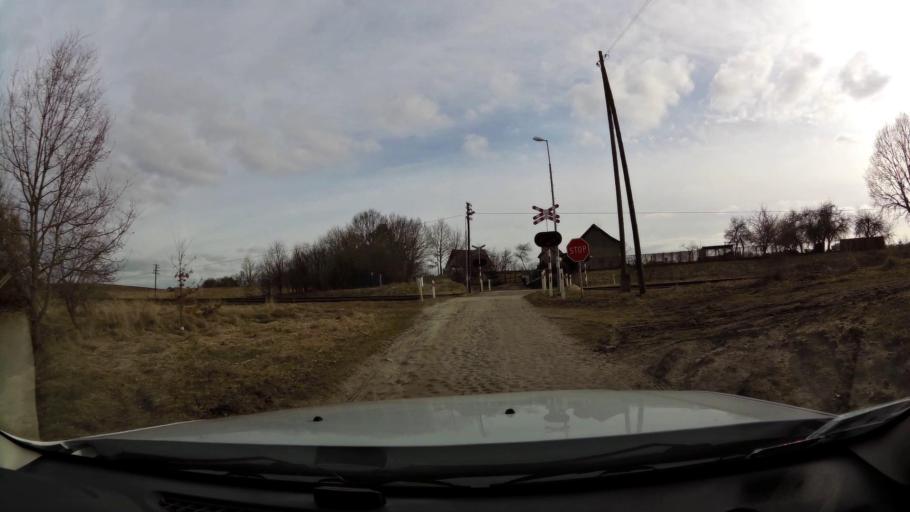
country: PL
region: West Pomeranian Voivodeship
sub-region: Powiat drawski
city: Drawsko Pomorskie
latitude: 53.5137
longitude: 15.7502
